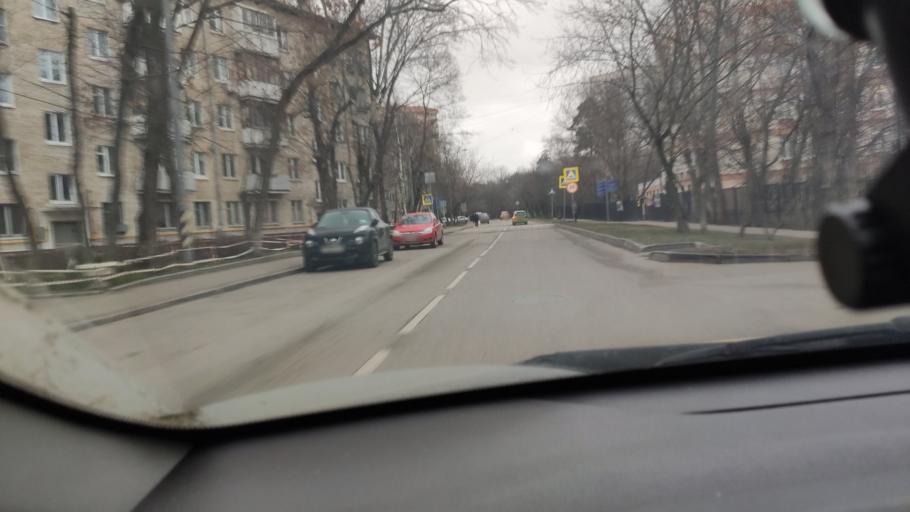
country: RU
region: Moscow
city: Tsaritsyno
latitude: 55.6234
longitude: 37.6639
